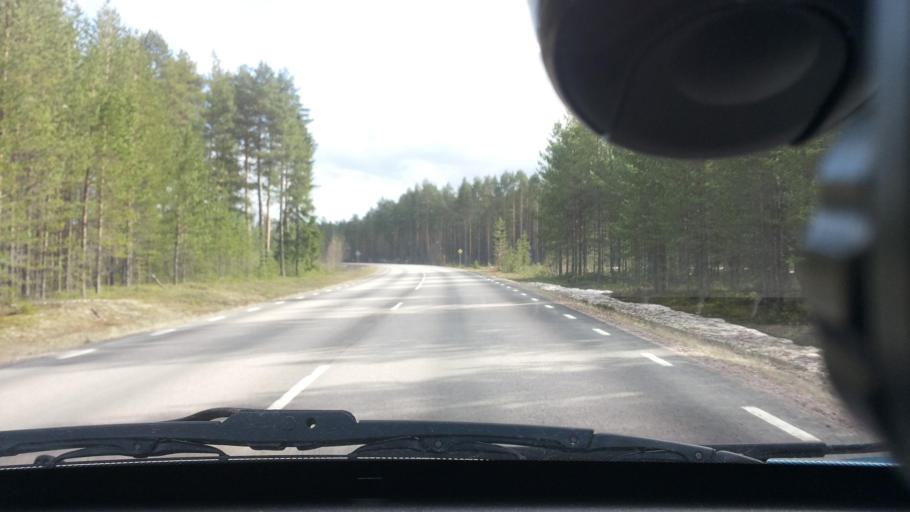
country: SE
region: Norrbotten
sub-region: Lulea Kommun
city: Sodra Sunderbyn
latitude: 65.6303
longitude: 21.9254
